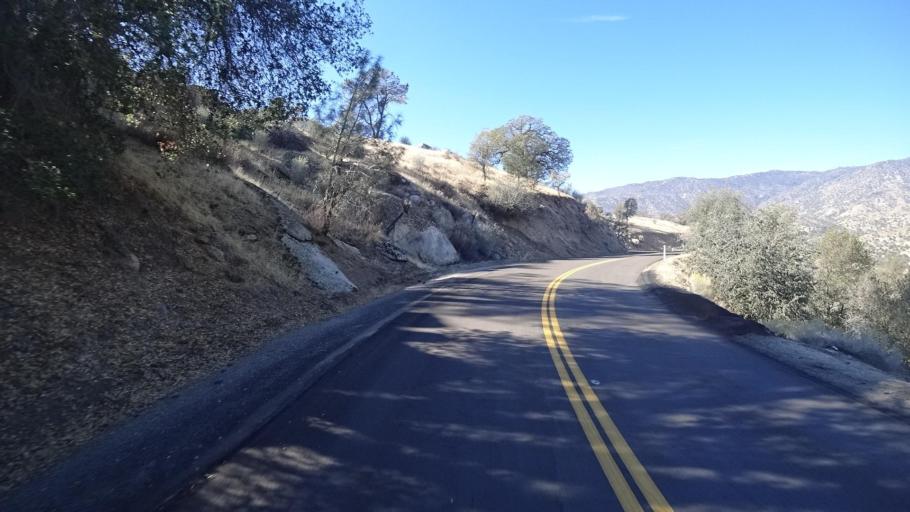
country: US
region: California
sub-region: Kern County
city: Bodfish
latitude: 35.5939
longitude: -118.5101
